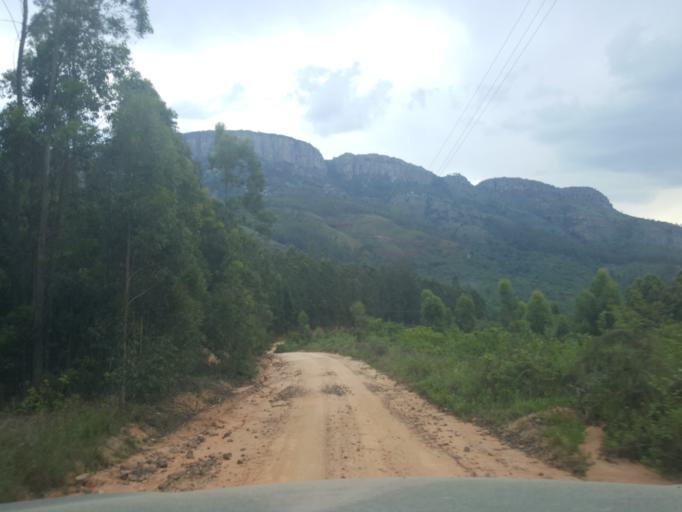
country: ZA
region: Limpopo
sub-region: Mopani District Municipality
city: Hoedspruit
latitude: -24.5921
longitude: 30.8705
